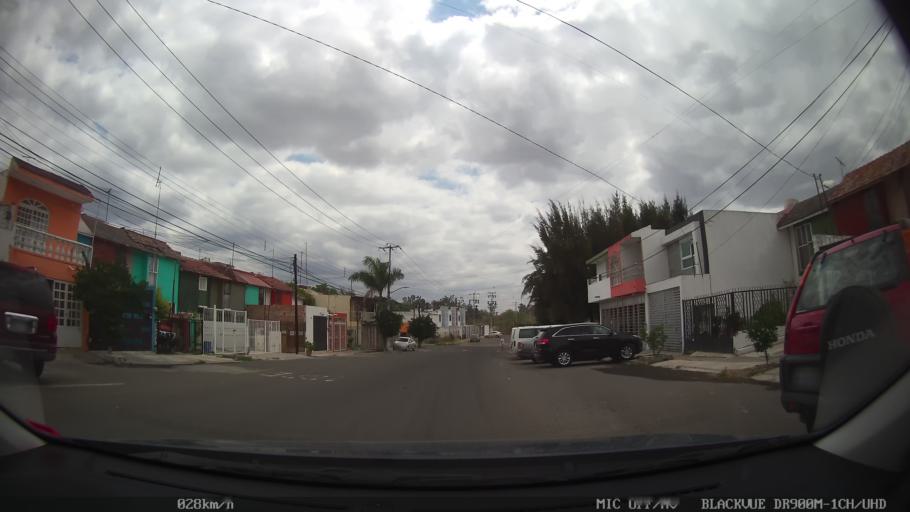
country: MX
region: Jalisco
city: Tonala
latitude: 20.6343
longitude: -103.2603
